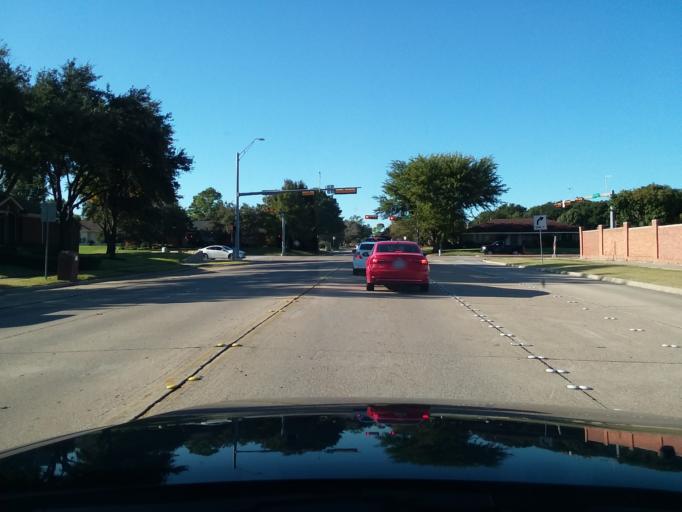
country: US
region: Texas
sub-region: Denton County
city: Lewisville
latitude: 33.0527
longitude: -97.0247
